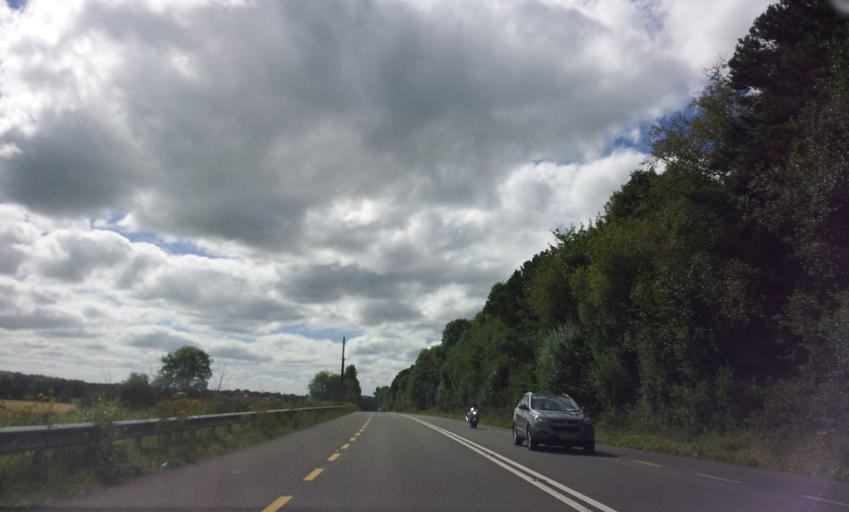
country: IE
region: Munster
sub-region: County Cork
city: Killumney
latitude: 51.8664
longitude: -8.7636
